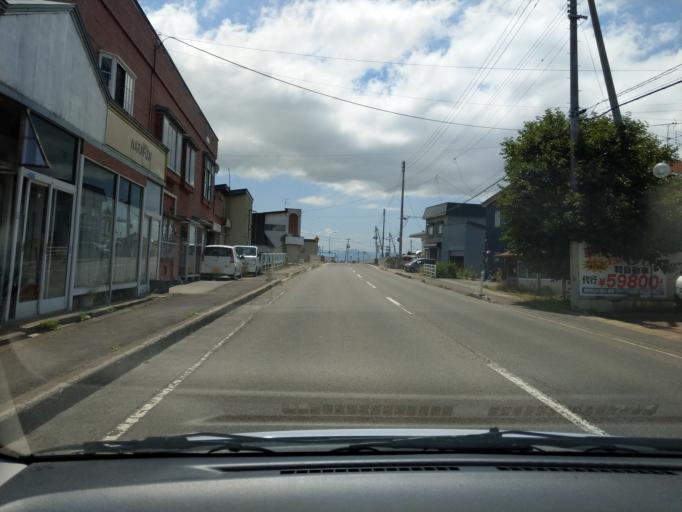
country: JP
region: Aomori
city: Namioka
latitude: 40.6856
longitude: 140.5554
